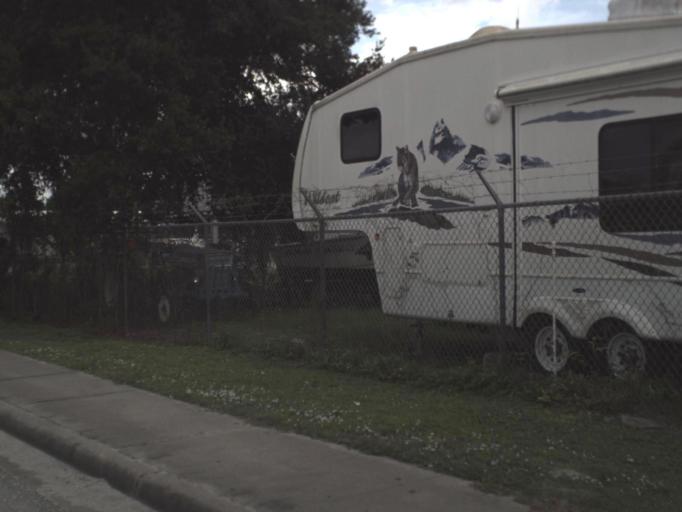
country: US
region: Florida
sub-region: Hendry County
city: LaBelle
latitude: 26.7569
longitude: -81.4374
